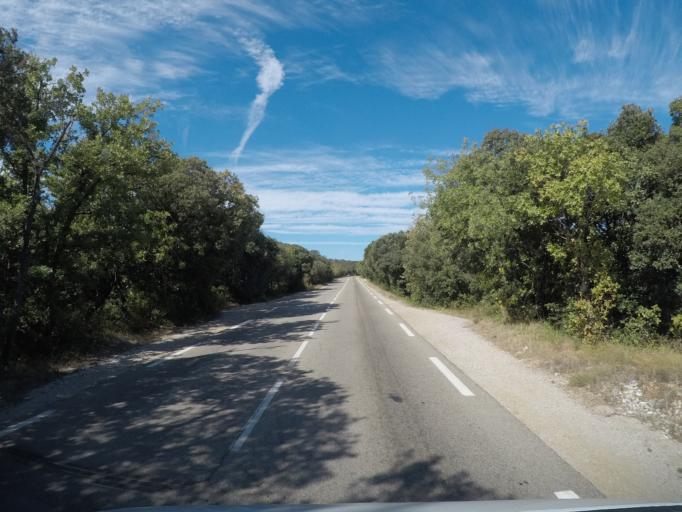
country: FR
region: Languedoc-Roussillon
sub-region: Departement de l'Herault
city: Saint-Martin-de-Londres
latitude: 43.7633
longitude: 3.7470
